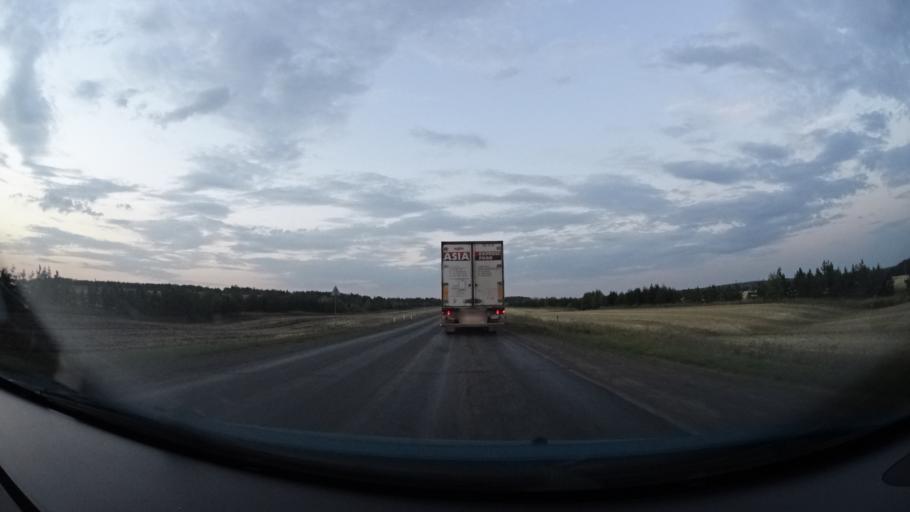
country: RU
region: Tatarstan
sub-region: Bavlinskiy Rayon
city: Bavly
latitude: 54.2779
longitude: 52.9868
